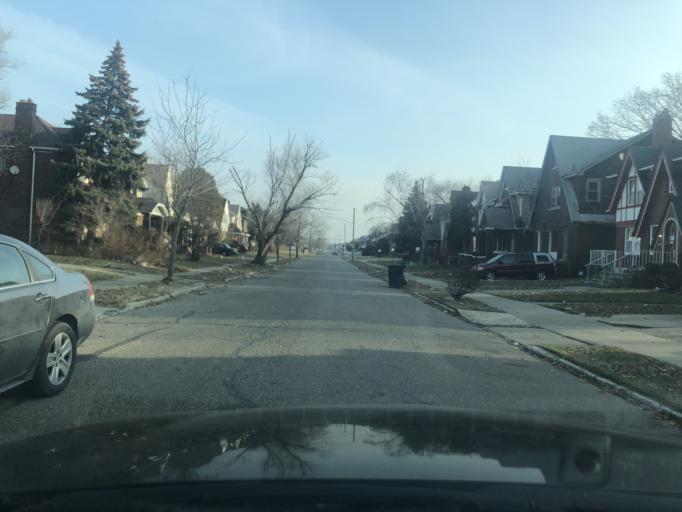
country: US
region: Michigan
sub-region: Wayne County
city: Highland Park
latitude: 42.3897
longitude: -83.1290
